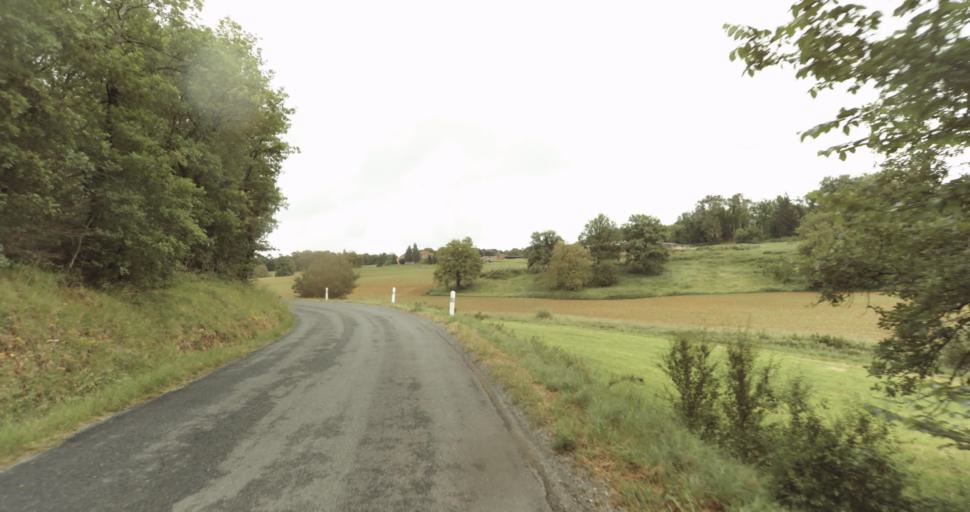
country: FR
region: Aquitaine
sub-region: Departement de la Dordogne
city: Belves
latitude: 44.7577
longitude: 0.9134
